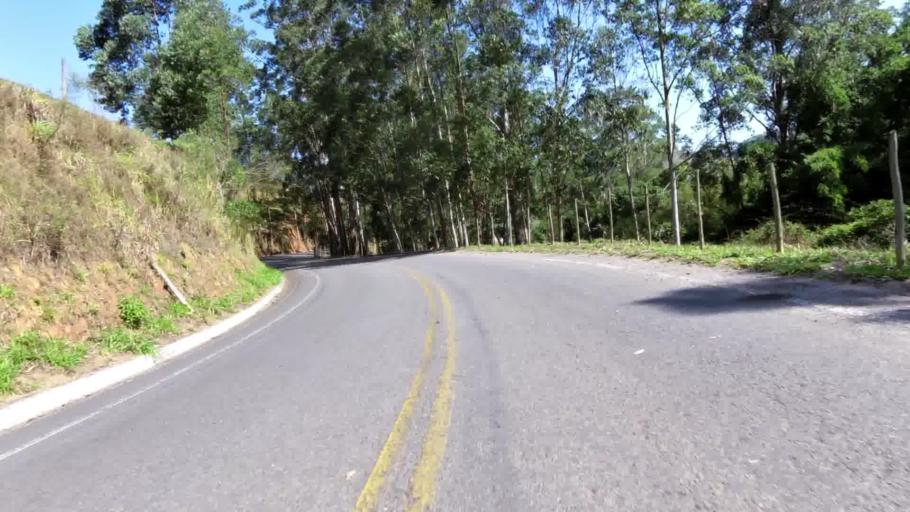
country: BR
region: Espirito Santo
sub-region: Alfredo Chaves
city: Alfredo Chaves
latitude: -20.5640
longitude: -40.8053
